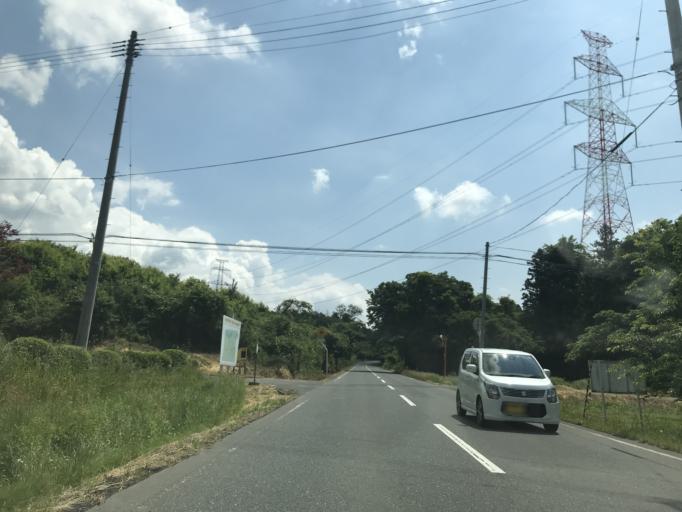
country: JP
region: Miyagi
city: Furukawa
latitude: 38.6218
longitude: 141.0077
